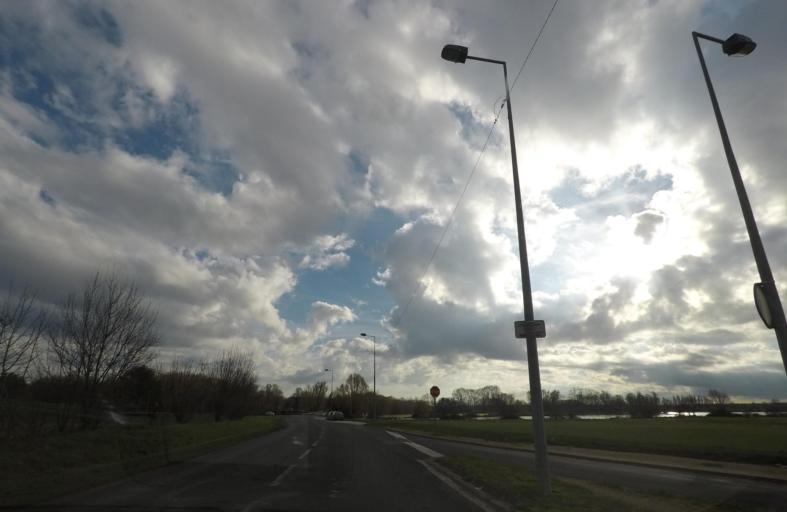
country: FR
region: Centre
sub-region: Departement du Cher
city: Bourges
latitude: 47.0506
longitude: 2.4072
